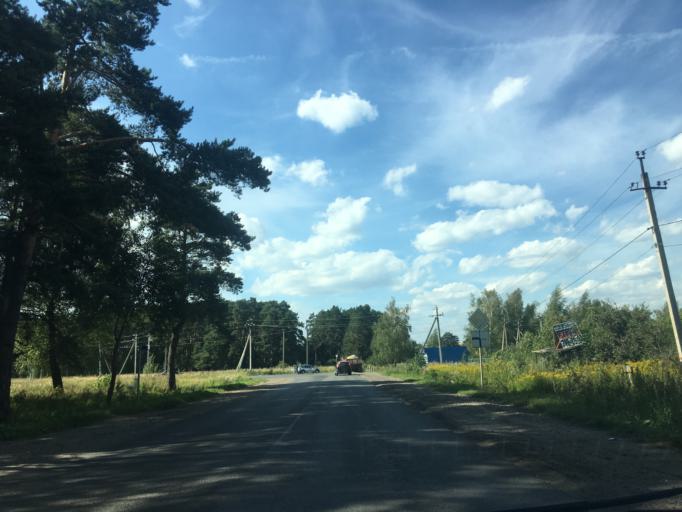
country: RU
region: Moscow
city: Zagor'ye
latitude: 55.5321
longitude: 37.6660
